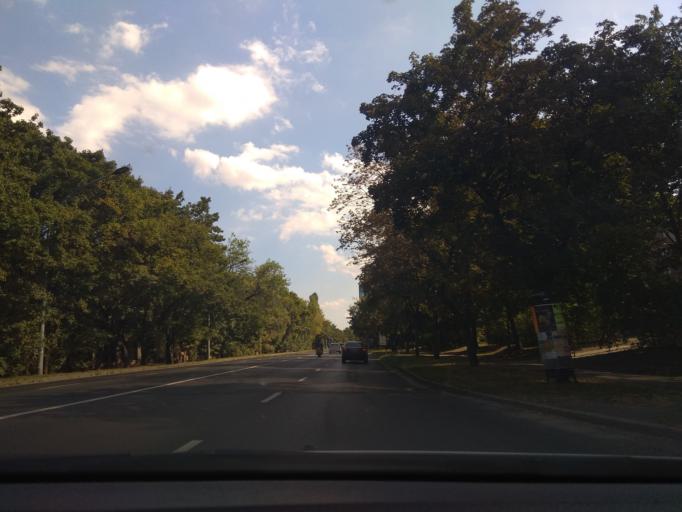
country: HU
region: Borsod-Abauj-Zemplen
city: Miskolc
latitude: 48.1195
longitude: 20.7883
